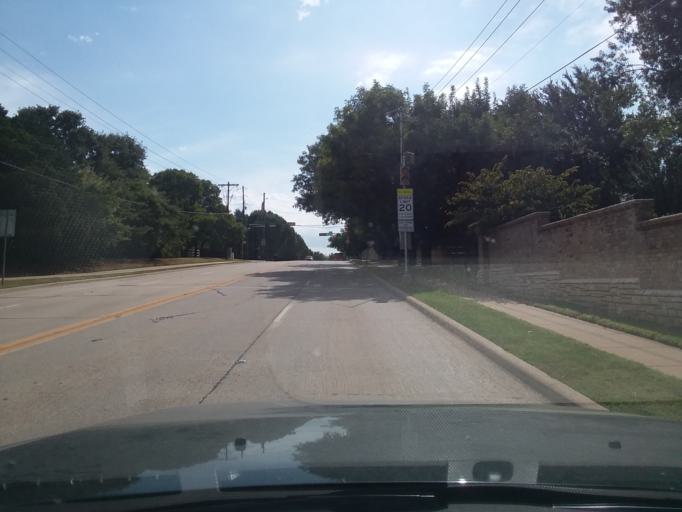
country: US
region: Texas
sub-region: Denton County
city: Flower Mound
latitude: 33.0137
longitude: -97.0806
